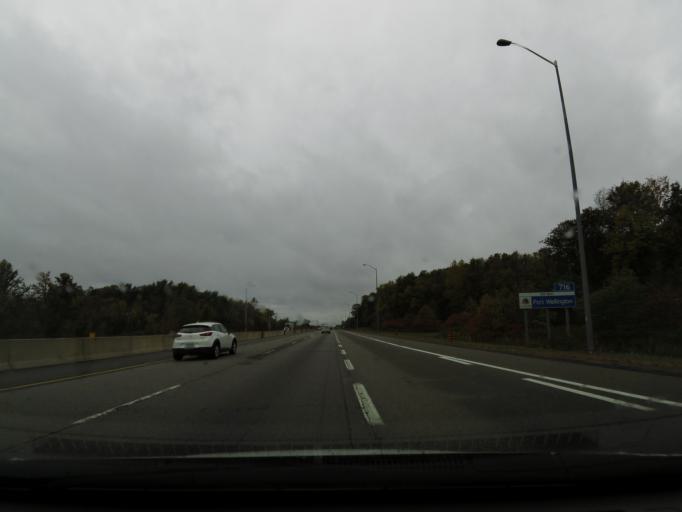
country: CA
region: Ontario
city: Prescott
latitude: 44.7414
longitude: -75.4978
